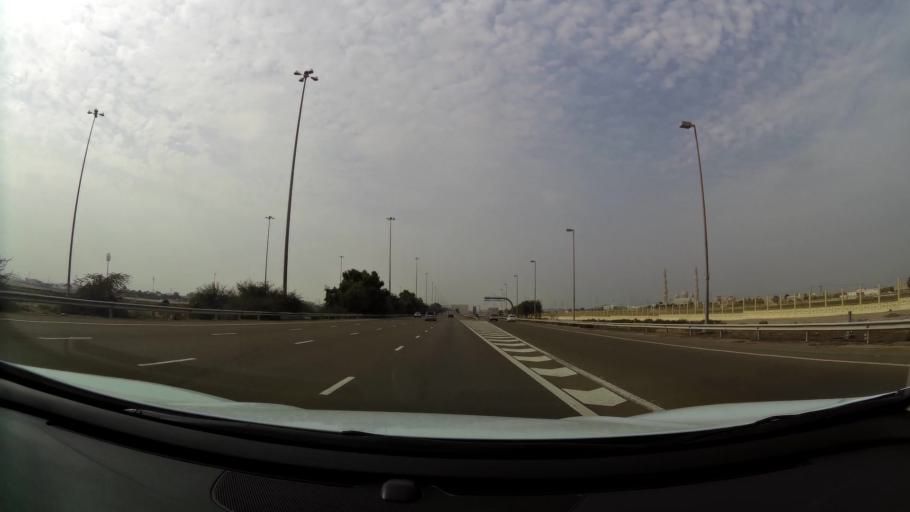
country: AE
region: Abu Dhabi
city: Abu Dhabi
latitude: 24.6749
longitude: 54.7638
